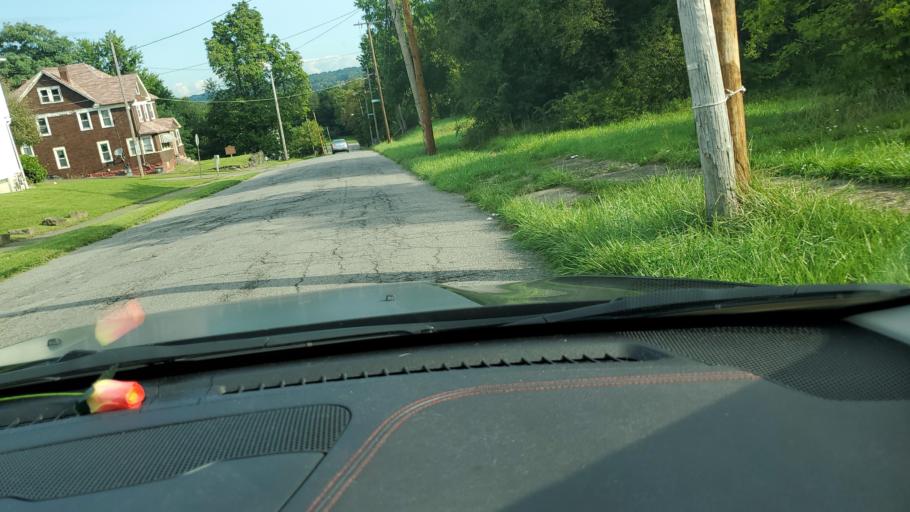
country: US
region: Ohio
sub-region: Mahoning County
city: Youngstown
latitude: 41.0948
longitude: -80.6666
